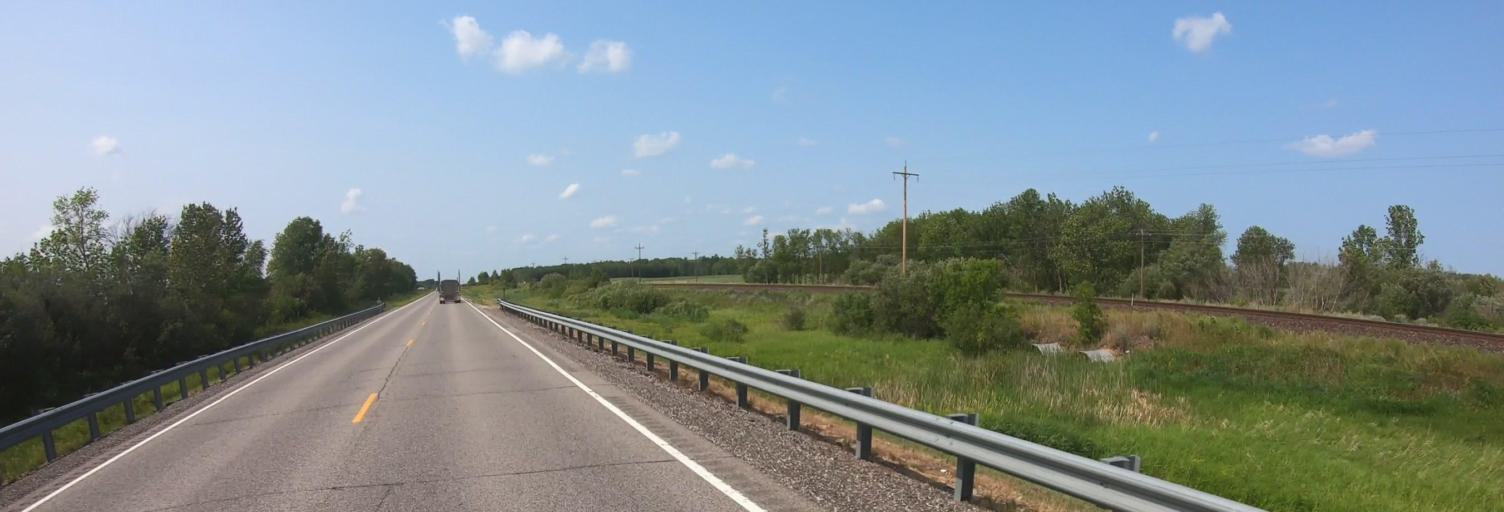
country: US
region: Minnesota
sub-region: Roseau County
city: Warroad
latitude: 48.8304
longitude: -95.1661
